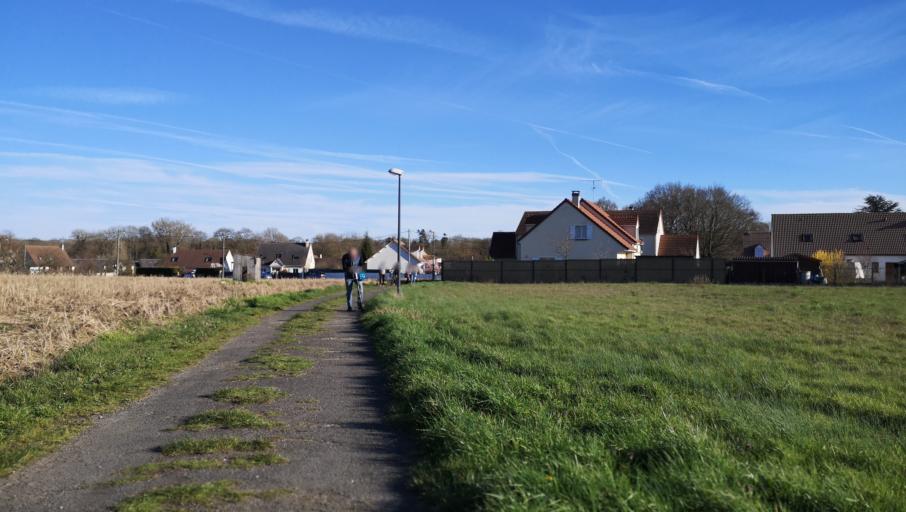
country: FR
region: Centre
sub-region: Departement du Loiret
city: Saint-Jean-de-Braye
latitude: 47.9160
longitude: 1.9915
